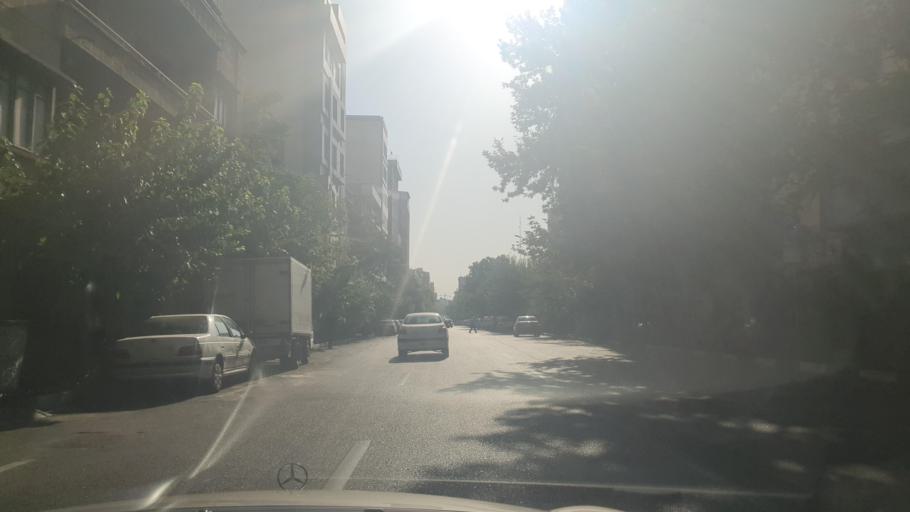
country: IR
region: Tehran
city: Tehran
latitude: 35.7057
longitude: 51.4252
